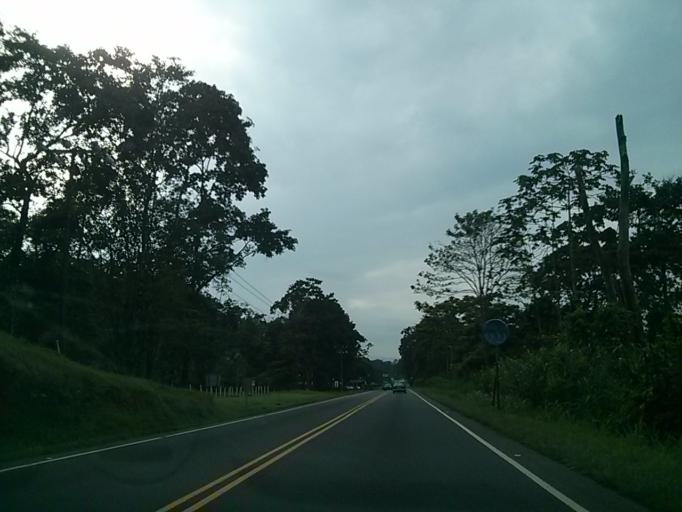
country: CR
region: Limon
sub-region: Canton de Pococi
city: Guapiles
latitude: 10.2070
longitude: -83.8285
